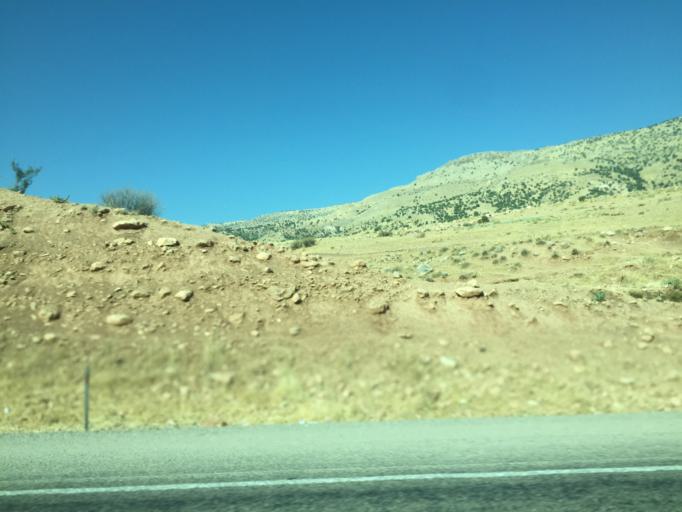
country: TR
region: Batman
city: Hasankeyf
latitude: 37.6739
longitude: 41.4546
